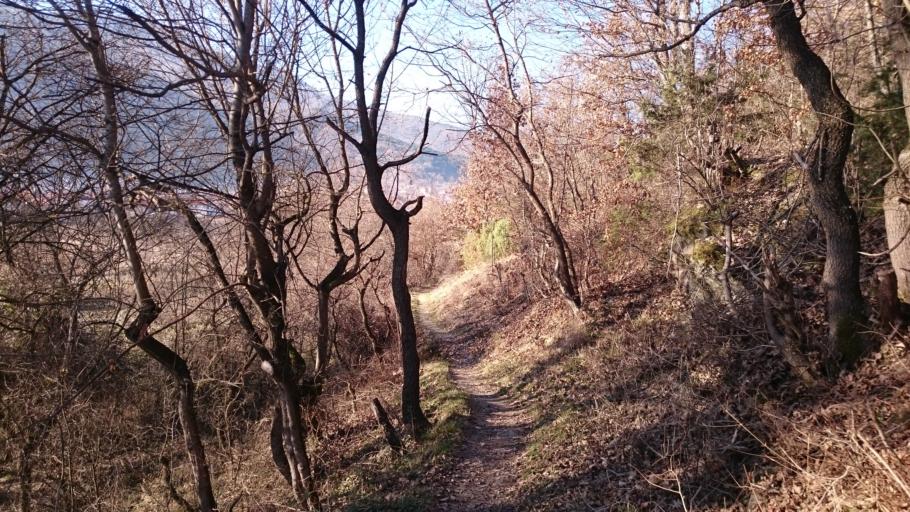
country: MK
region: Makedonski Brod
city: Makedonski Brod
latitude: 41.5133
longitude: 21.2243
